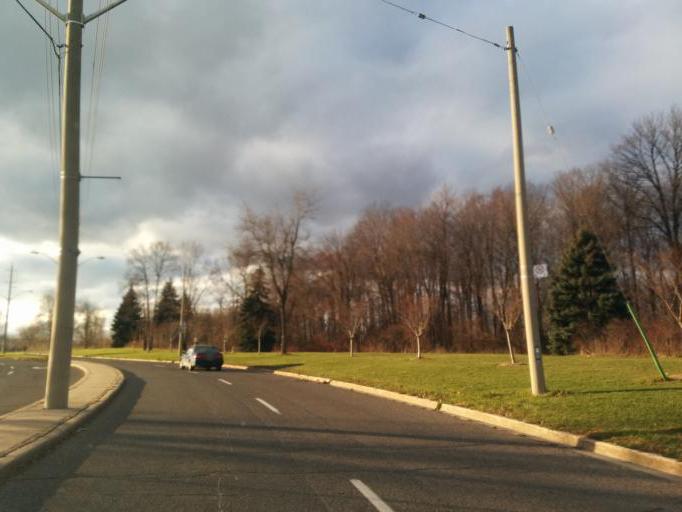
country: CA
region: Ontario
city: Etobicoke
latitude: 43.6458
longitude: -79.5906
